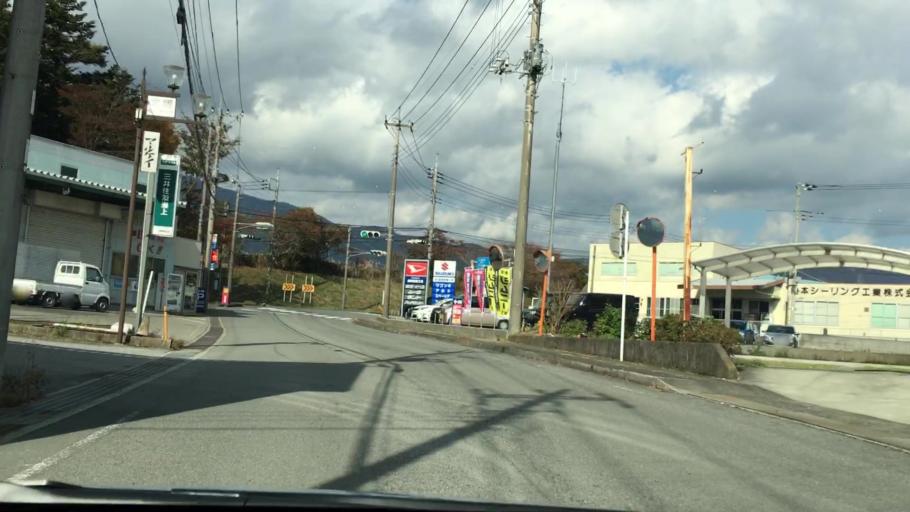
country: JP
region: Shizuoka
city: Gotemba
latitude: 35.3549
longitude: 138.9446
